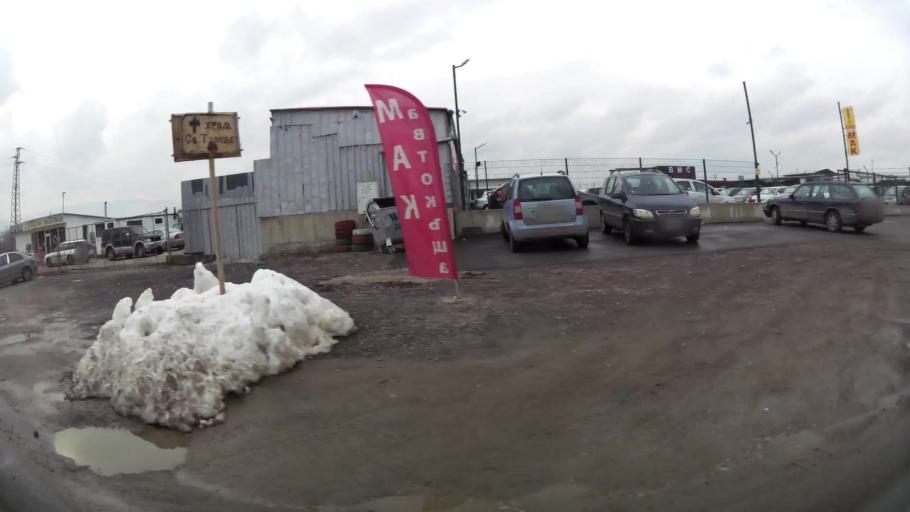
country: BG
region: Sofiya
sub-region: Obshtina Bozhurishte
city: Bozhurishte
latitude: 42.7036
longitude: 23.2303
